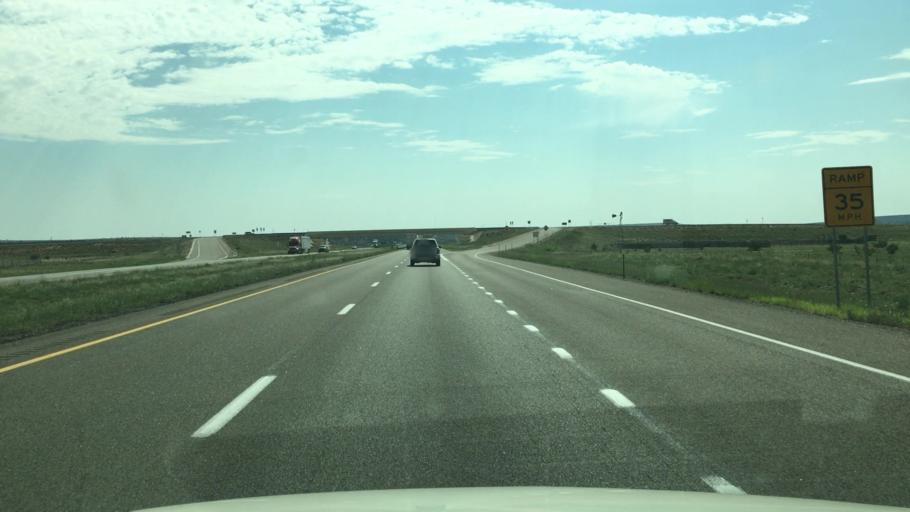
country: US
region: New Mexico
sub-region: Guadalupe County
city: Santa Rosa
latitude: 34.9765
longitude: -104.9954
